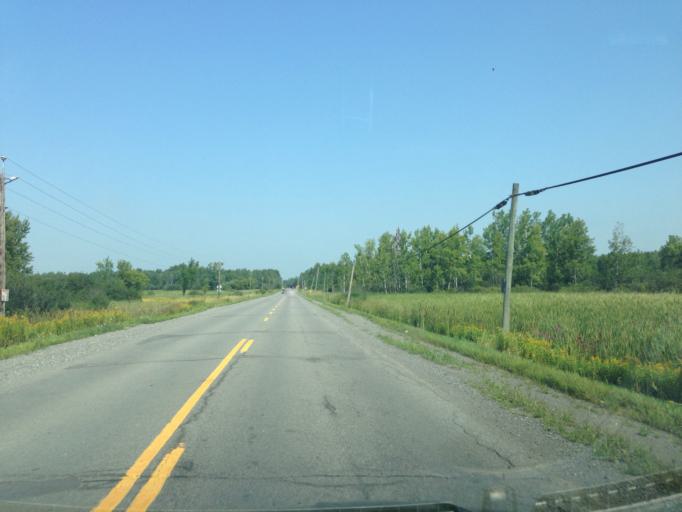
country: CA
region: Ontario
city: Ottawa
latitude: 45.4123
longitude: -75.5632
